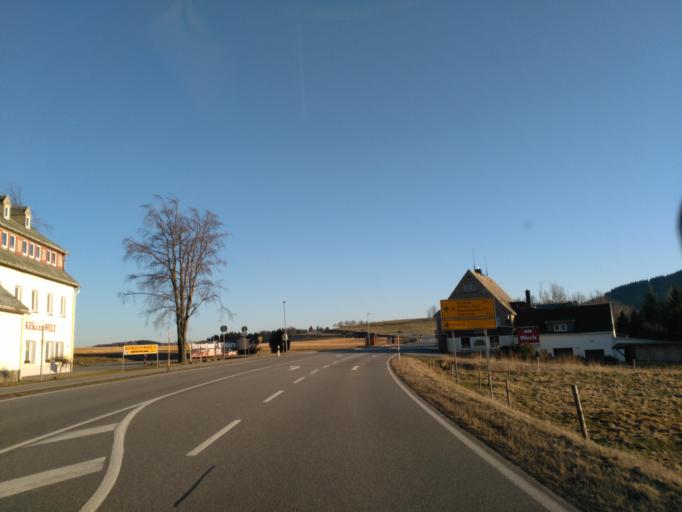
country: DE
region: Saxony
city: Barenstein
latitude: 50.5235
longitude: 13.0310
